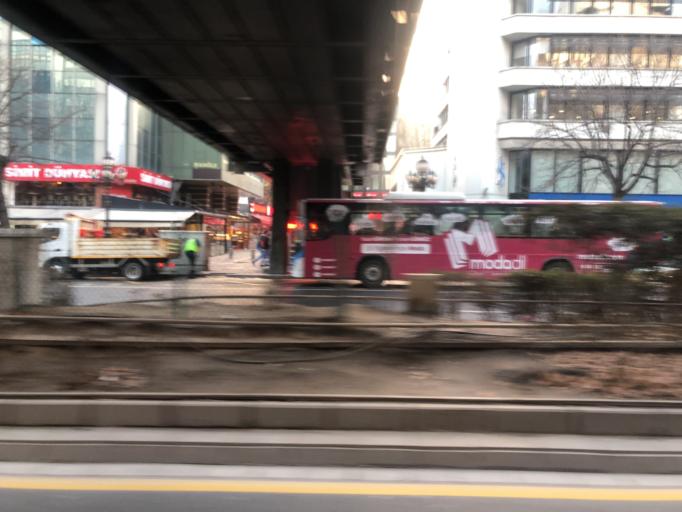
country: TR
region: Ankara
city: Ankara
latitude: 39.9232
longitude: 32.8542
